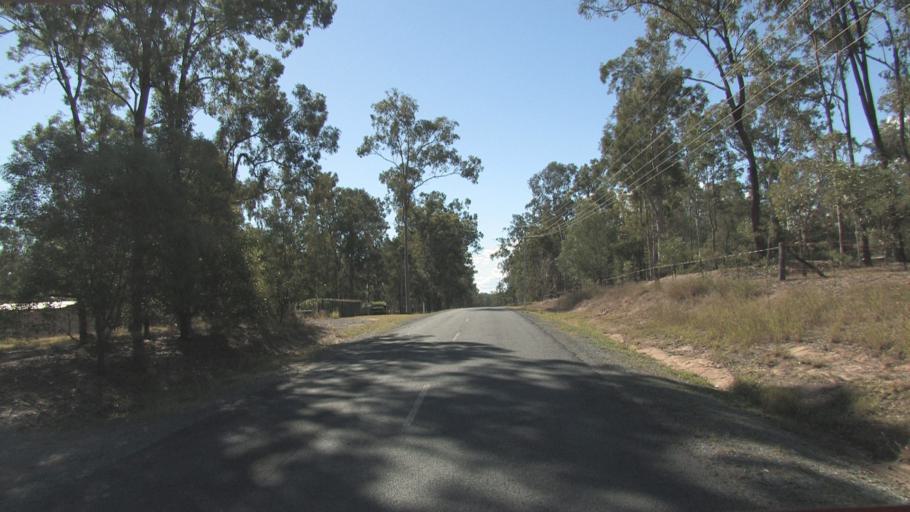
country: AU
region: Queensland
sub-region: Logan
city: Chambers Flat
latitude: -27.8117
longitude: 153.0717
